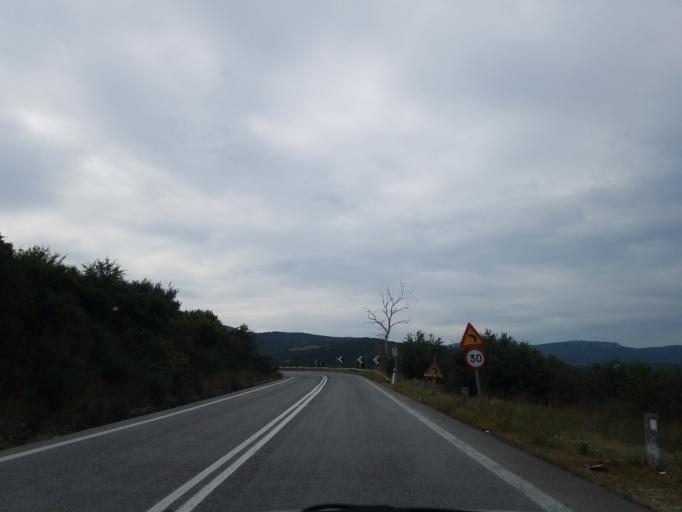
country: GR
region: Central Greece
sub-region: Nomos Fthiotidos
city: Domokos
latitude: 39.1519
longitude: 22.2975
